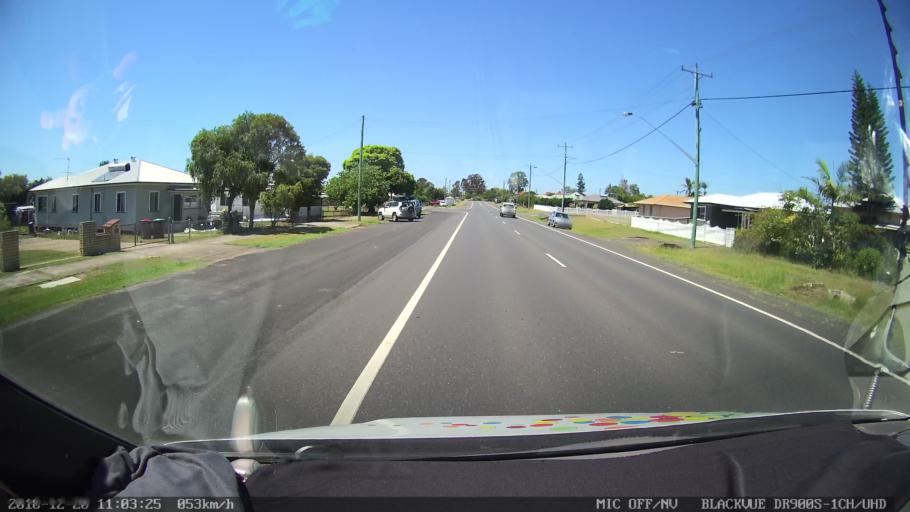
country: AU
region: New South Wales
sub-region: Richmond Valley
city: Casino
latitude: -28.8769
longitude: 153.0431
